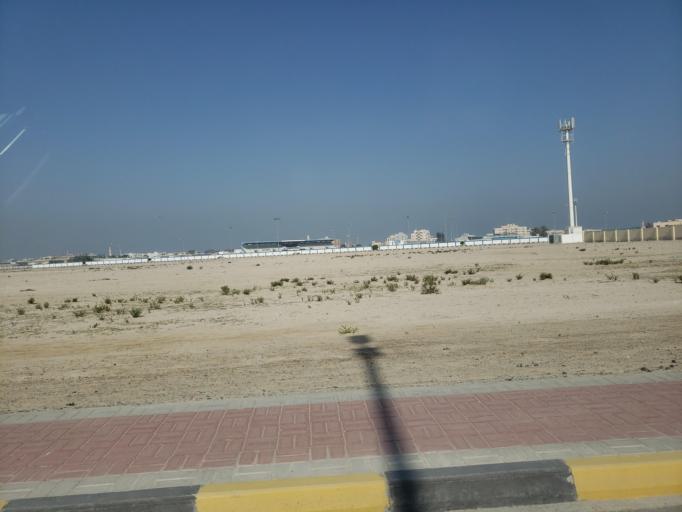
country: AE
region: Umm al Qaywayn
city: Umm al Qaywayn
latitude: 25.5656
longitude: 55.5643
